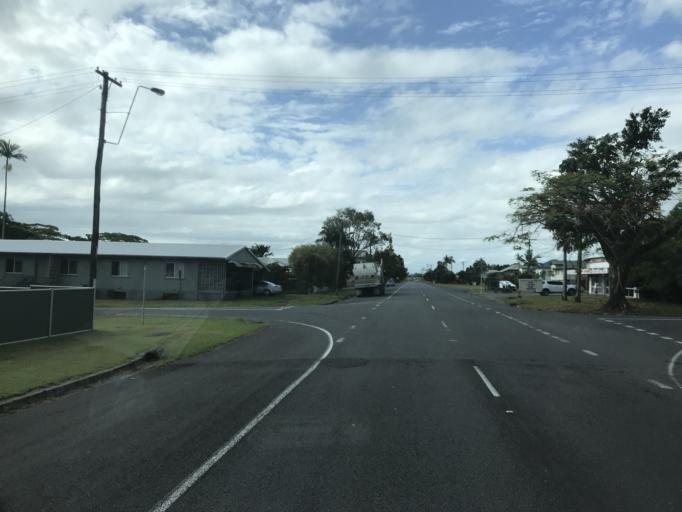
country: AU
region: Queensland
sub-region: Cassowary Coast
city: Innisfail
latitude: -17.5411
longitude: 146.0327
